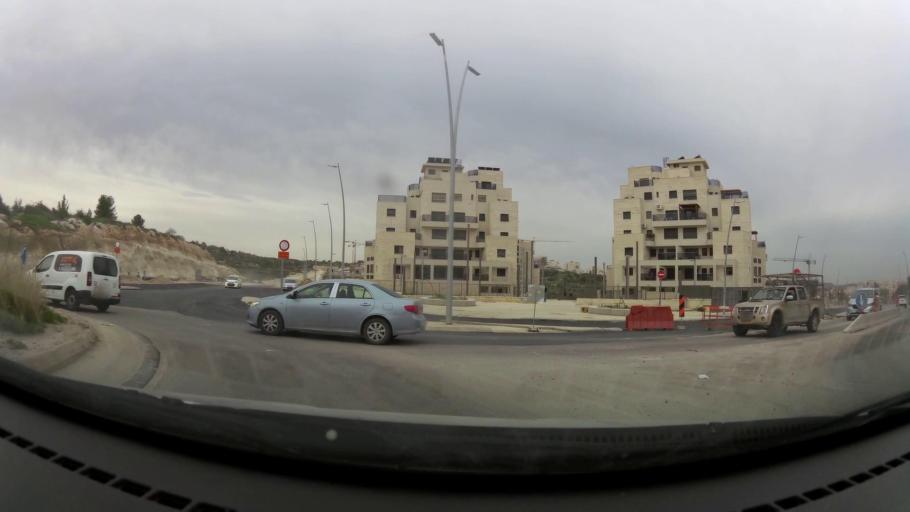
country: IL
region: Jerusalem
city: Bet Shemesh
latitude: 31.7055
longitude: 35.0029
